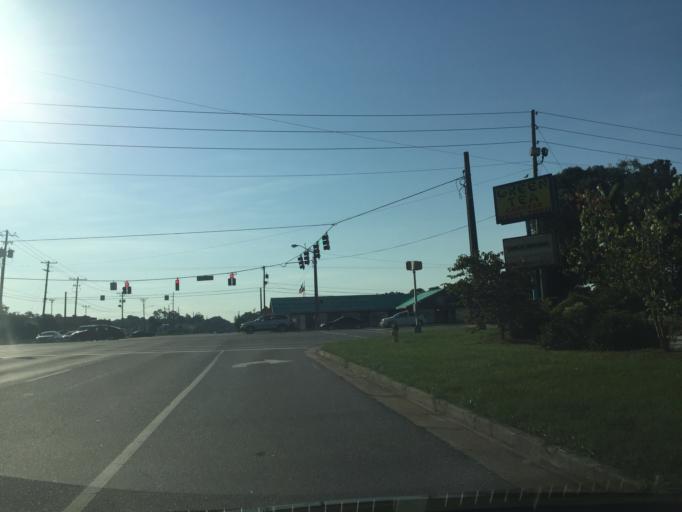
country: US
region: Georgia
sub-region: Chatham County
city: Isle of Hope
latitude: 32.0066
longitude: -81.1015
